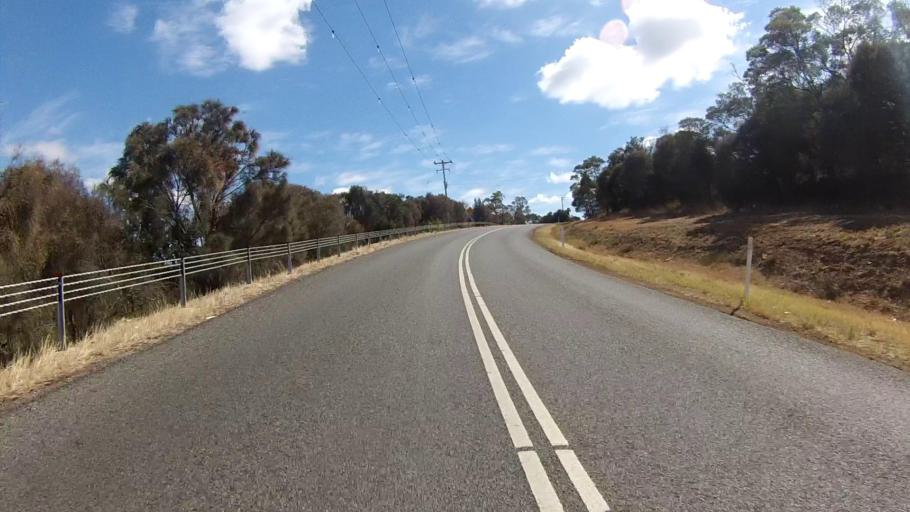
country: AU
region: Tasmania
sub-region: Brighton
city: Bridgewater
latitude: -42.7089
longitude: 147.2690
